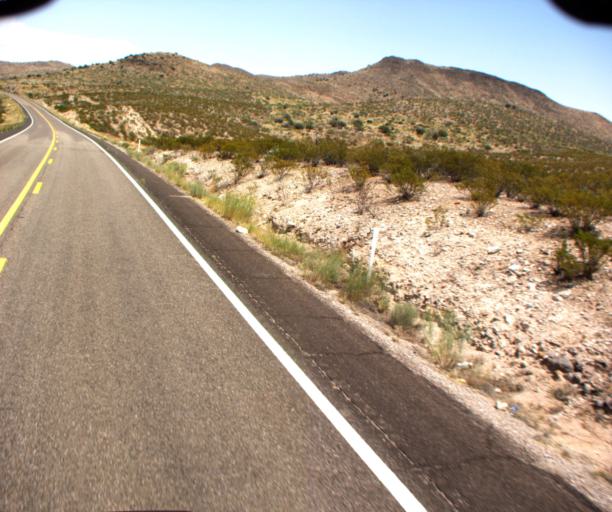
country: US
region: Arizona
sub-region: Greenlee County
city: Clifton
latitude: 32.7535
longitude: -109.3327
